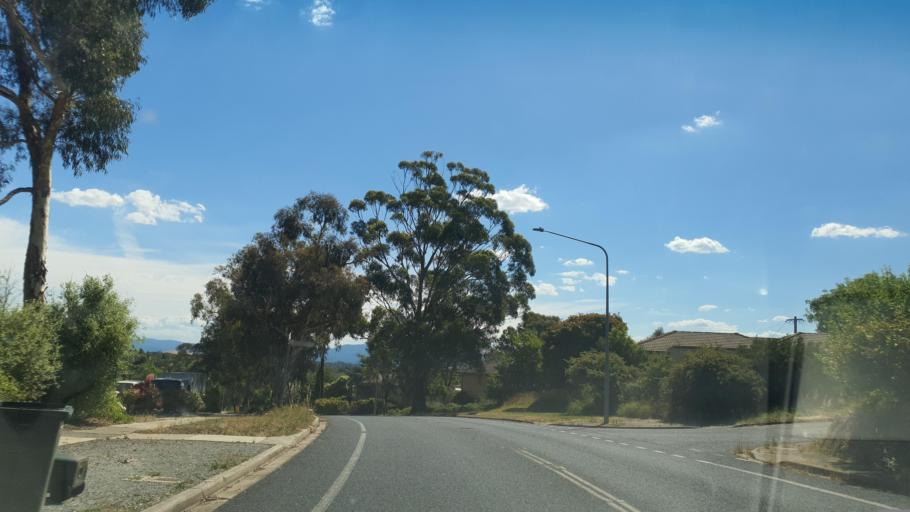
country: AU
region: Australian Capital Territory
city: Belconnen
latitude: -35.2080
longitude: 149.0403
